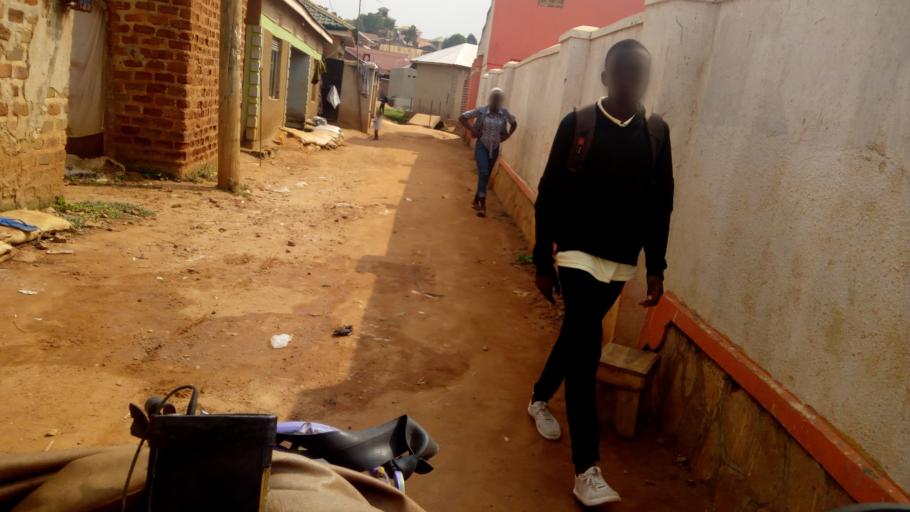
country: UG
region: Central Region
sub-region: Wakiso District
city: Kireka
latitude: 0.3235
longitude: 32.6522
